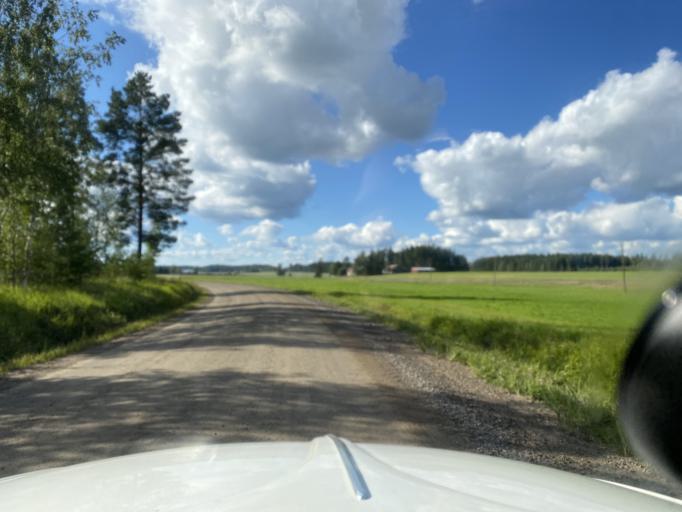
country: FI
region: Pirkanmaa
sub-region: Lounais-Pirkanmaa
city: Punkalaidun
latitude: 61.1259
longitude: 23.2574
